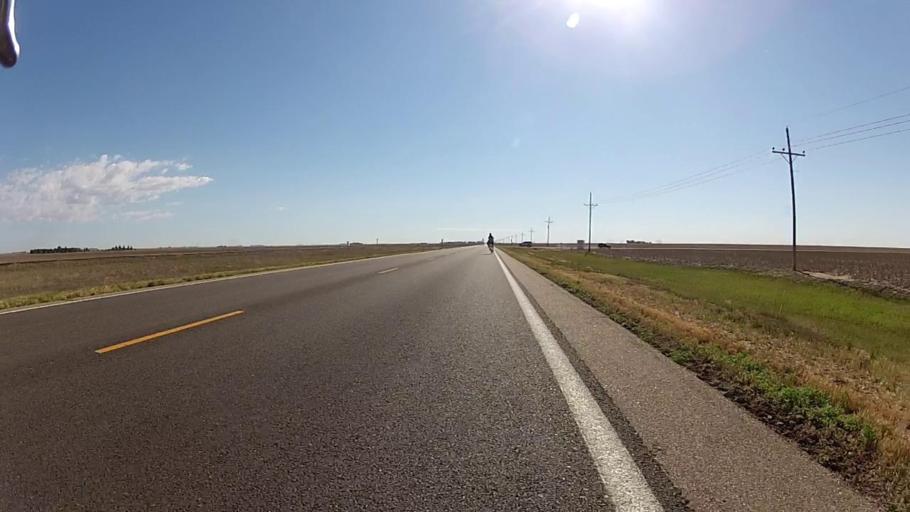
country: US
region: Kansas
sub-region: Gray County
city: Cimarron
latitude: 37.5808
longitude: -100.5085
